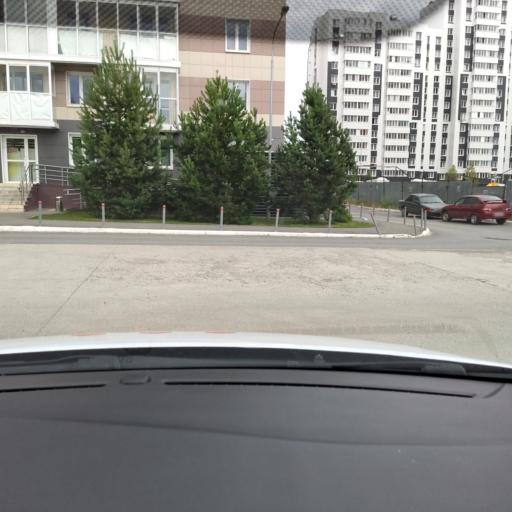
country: RU
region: Tatarstan
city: Osinovo
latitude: 55.8459
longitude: 48.9051
